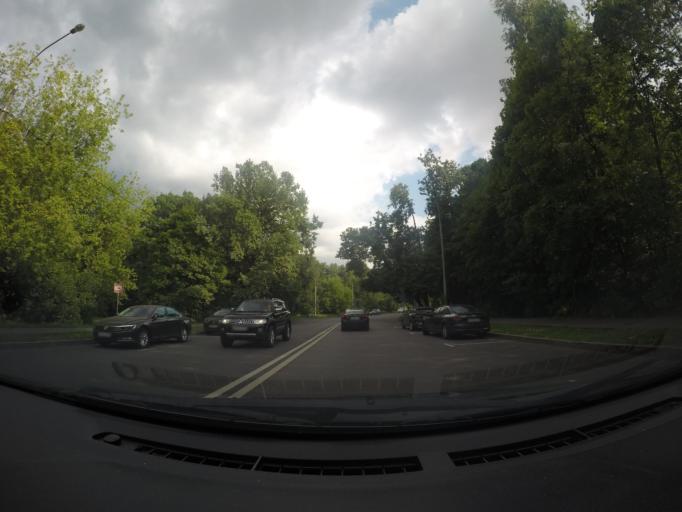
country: RU
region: Moscow
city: Sokol'niki
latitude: 55.8013
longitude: 37.6862
